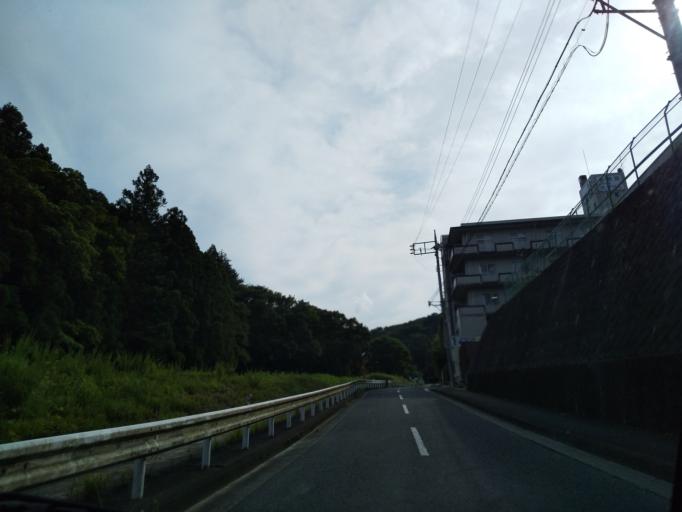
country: JP
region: Kanagawa
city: Atsugi
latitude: 35.4883
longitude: 139.3089
